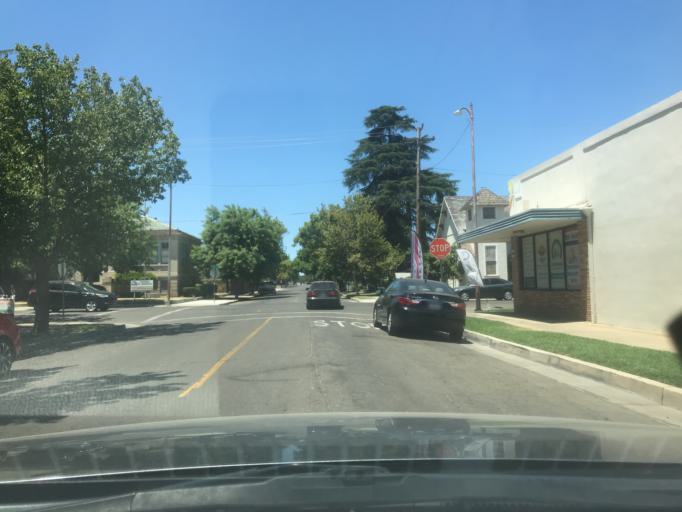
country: US
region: California
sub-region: Merced County
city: Atwater
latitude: 37.3475
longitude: -120.6081
